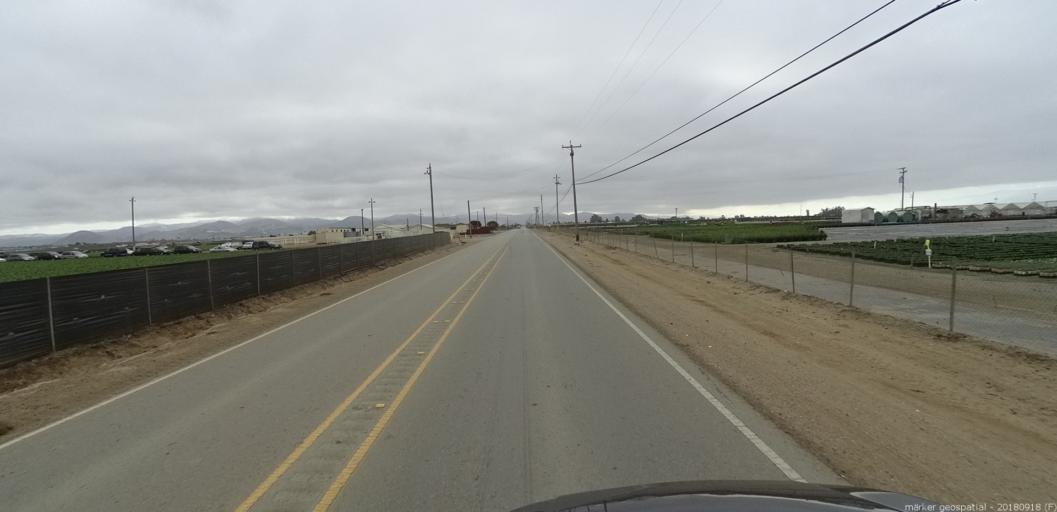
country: US
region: California
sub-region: Monterey County
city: Prunedale
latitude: 36.7397
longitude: -121.6749
